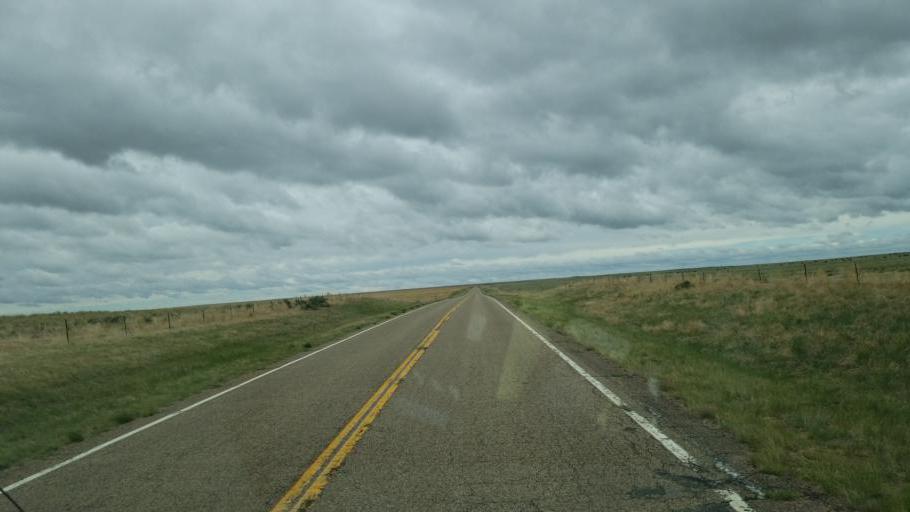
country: US
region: Colorado
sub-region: Lincoln County
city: Hugo
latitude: 38.8509
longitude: -103.5870
